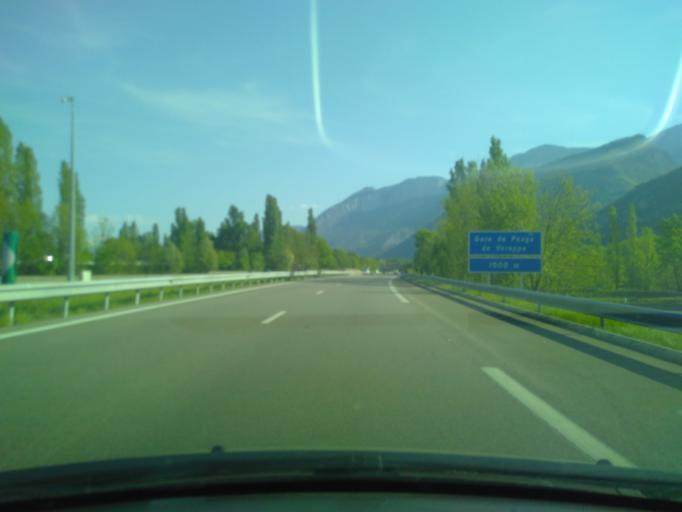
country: FR
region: Rhone-Alpes
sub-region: Departement de l'Isere
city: Voreppe
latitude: 45.2961
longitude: 5.6203
